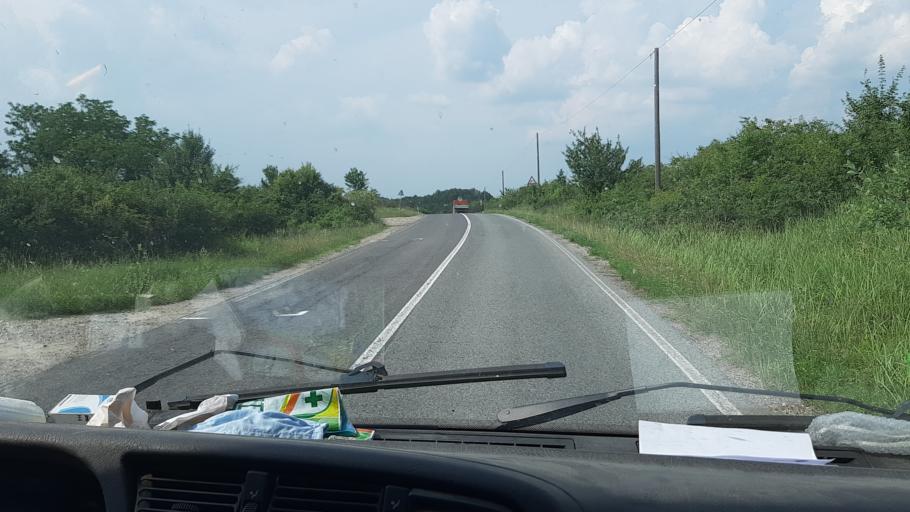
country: RO
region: Caras-Severin
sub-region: Comuna Farliug
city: Farliug
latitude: 45.5200
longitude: 21.8732
